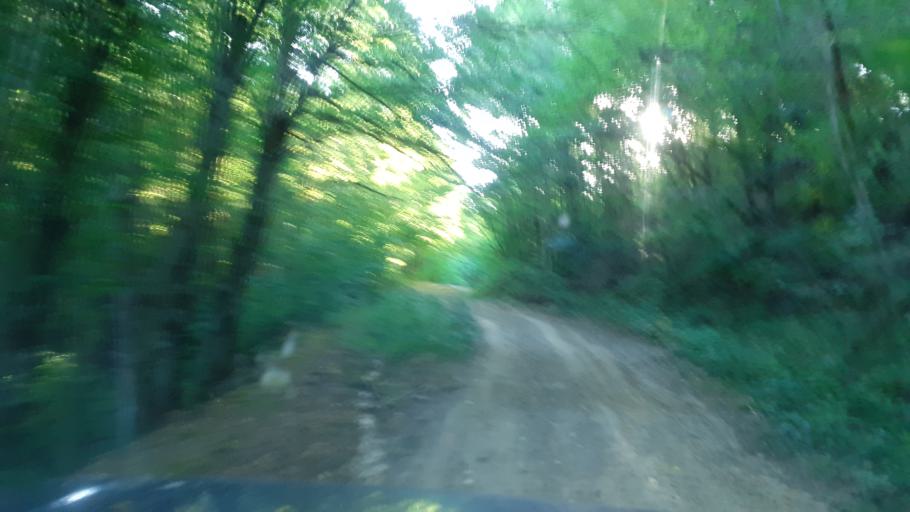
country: RU
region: Krasnodarskiy
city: Pshada
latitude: 44.6561
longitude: 38.4555
